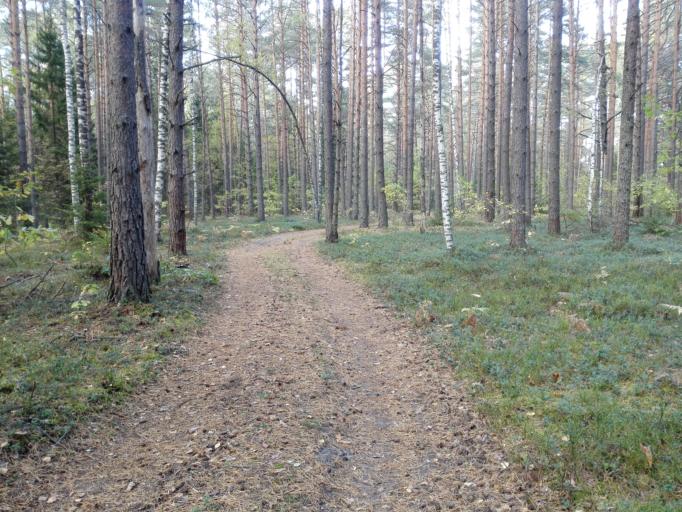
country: RU
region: Vladimir
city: Kommunar
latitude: 56.0754
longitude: 40.5130
